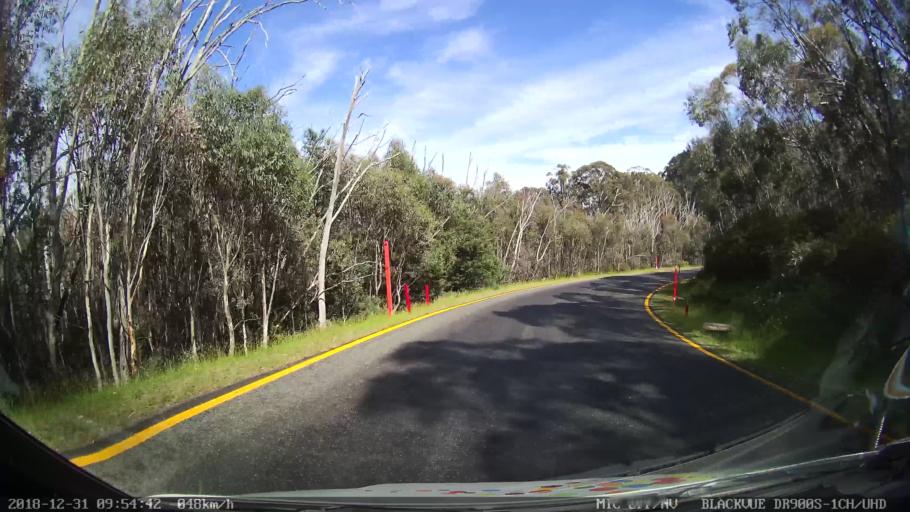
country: AU
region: New South Wales
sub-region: Snowy River
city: Jindabyne
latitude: -36.5343
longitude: 148.2338
